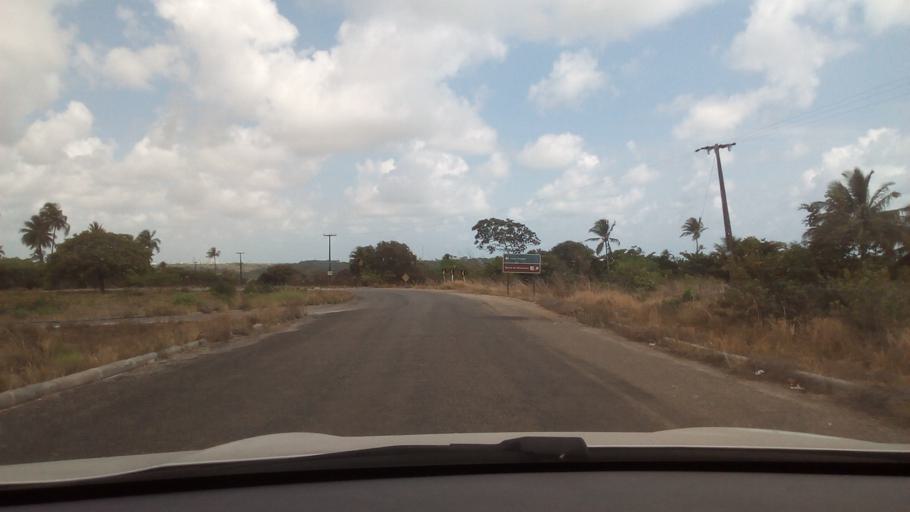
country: BR
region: Paraiba
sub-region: Conde
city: Conde
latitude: -7.2536
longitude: -34.8111
